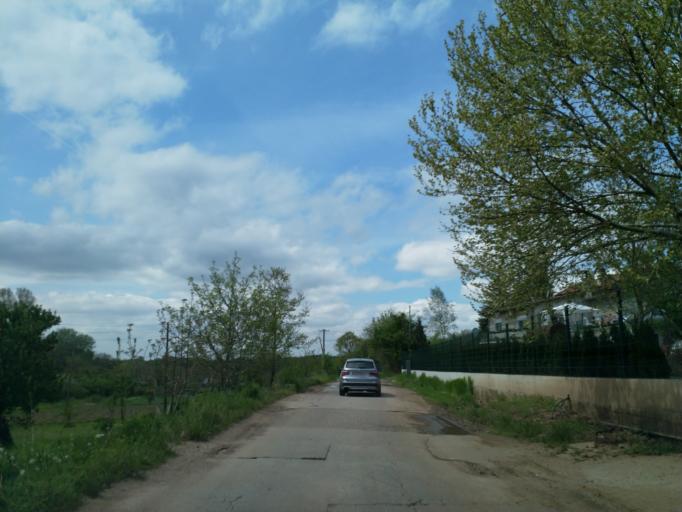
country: RS
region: Central Serbia
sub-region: Pomoravski Okrug
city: Cuprija
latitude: 43.9550
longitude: 21.4803
